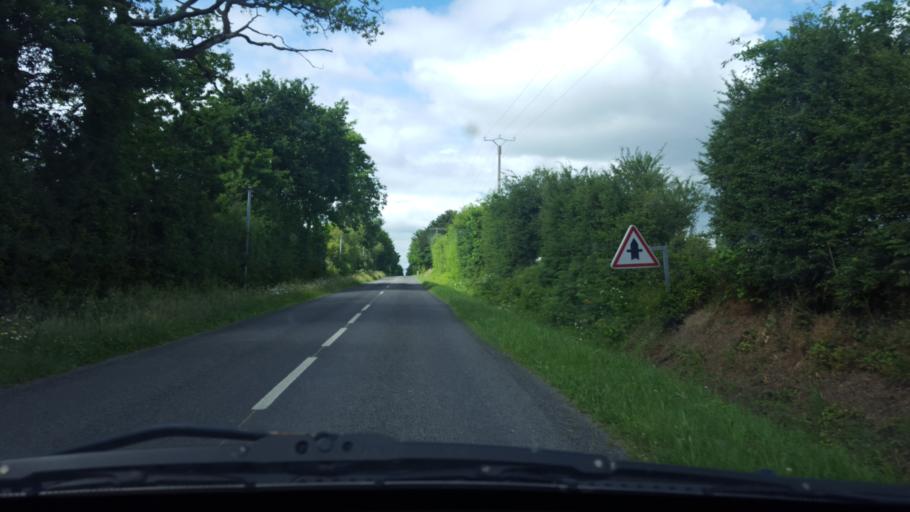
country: FR
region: Pays de la Loire
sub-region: Departement de la Loire-Atlantique
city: Saint-Lumine-de-Coutais
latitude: 47.0095
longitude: -1.7341
